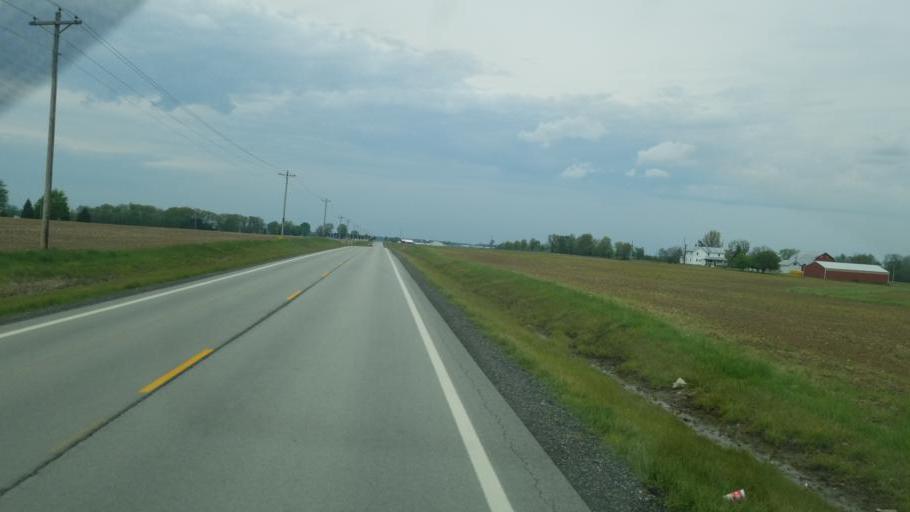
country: US
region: Ohio
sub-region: Huron County
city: Plymouth
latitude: 40.9717
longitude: -82.7434
